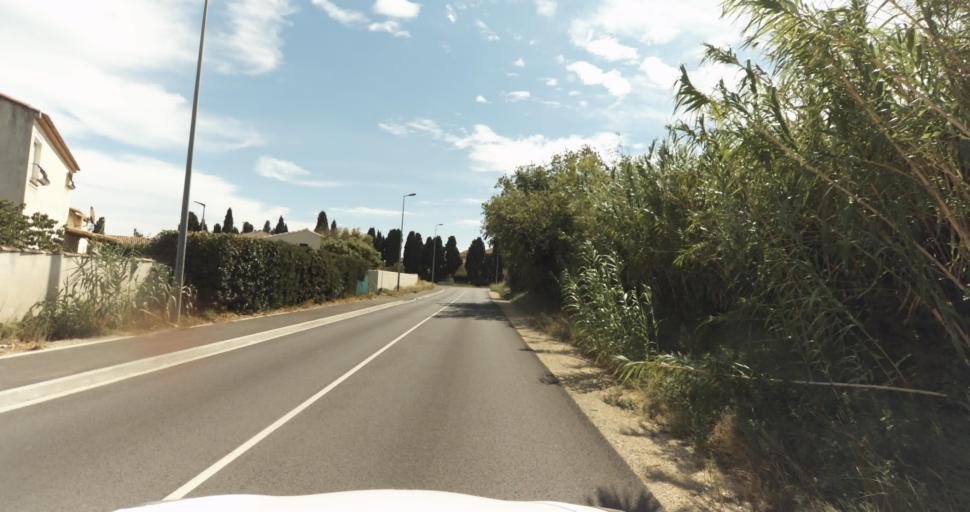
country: FR
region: Provence-Alpes-Cote d'Azur
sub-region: Departement des Bouches-du-Rhone
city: Miramas
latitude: 43.5867
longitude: 4.9955
